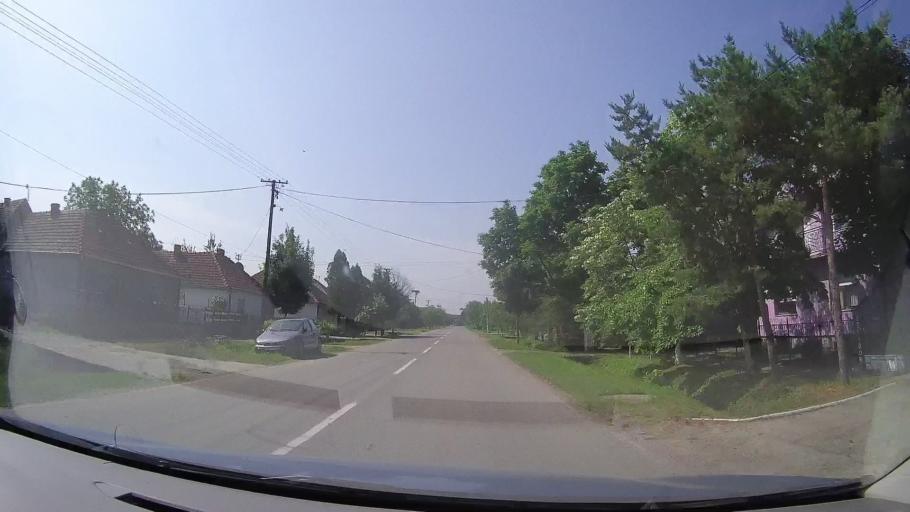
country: RS
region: Autonomna Pokrajina Vojvodina
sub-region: Srednjebanatski Okrug
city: Secanj
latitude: 45.3713
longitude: 20.7775
